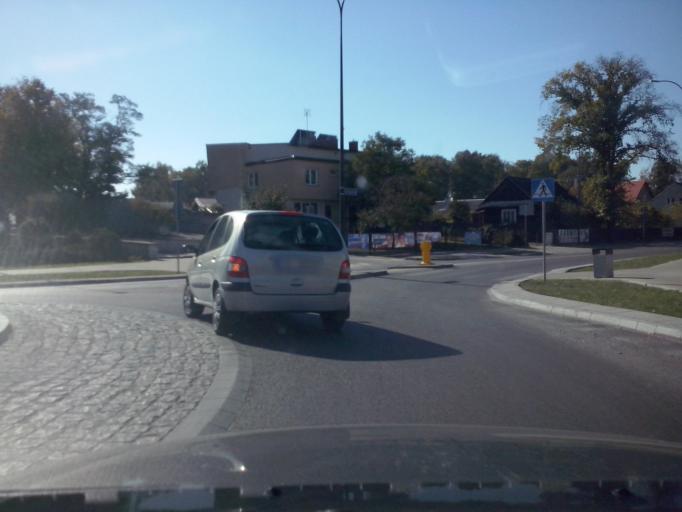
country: PL
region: Lublin Voivodeship
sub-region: Powiat bilgorajski
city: Bilgoraj
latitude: 50.5243
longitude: 22.7121
